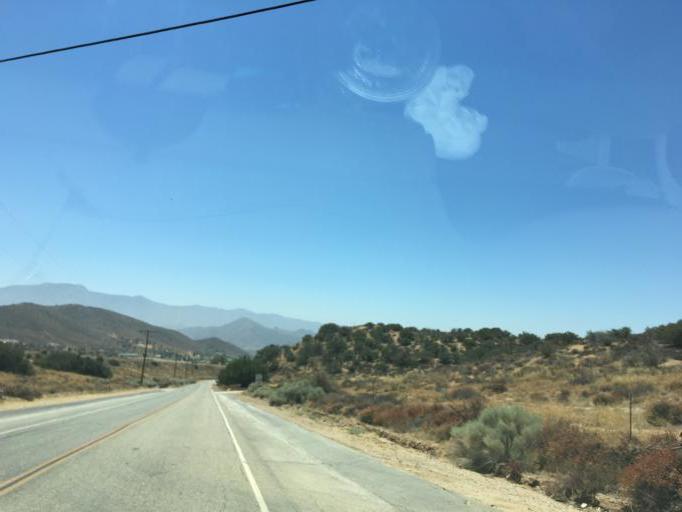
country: US
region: California
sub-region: Los Angeles County
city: Acton
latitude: 34.5244
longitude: -118.2114
